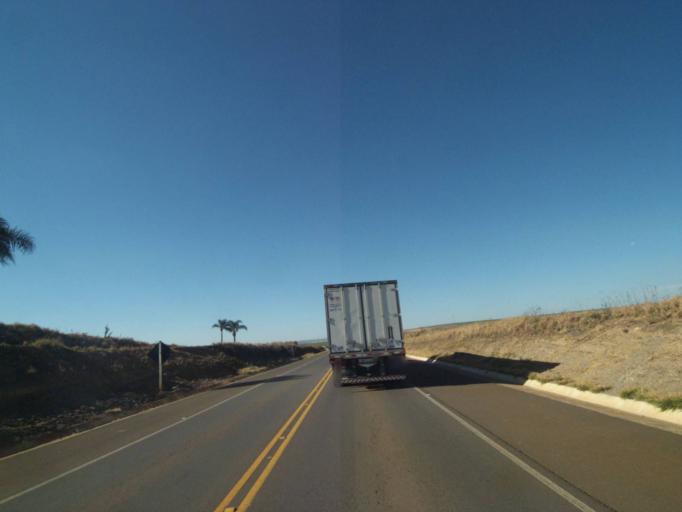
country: BR
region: Parana
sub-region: Tibagi
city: Tibagi
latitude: -24.6322
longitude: -50.4582
